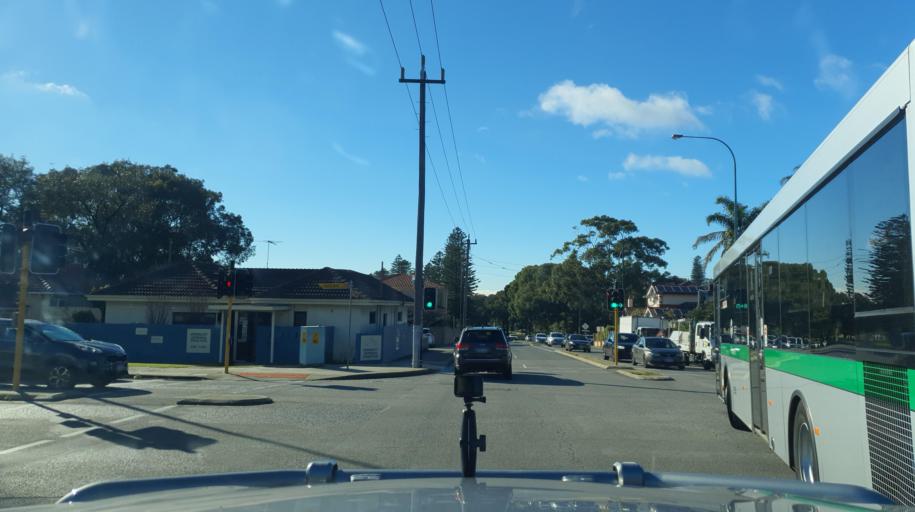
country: AU
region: Western Australia
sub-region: Cambridge
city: West Leederville
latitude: -31.9343
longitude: 115.8198
